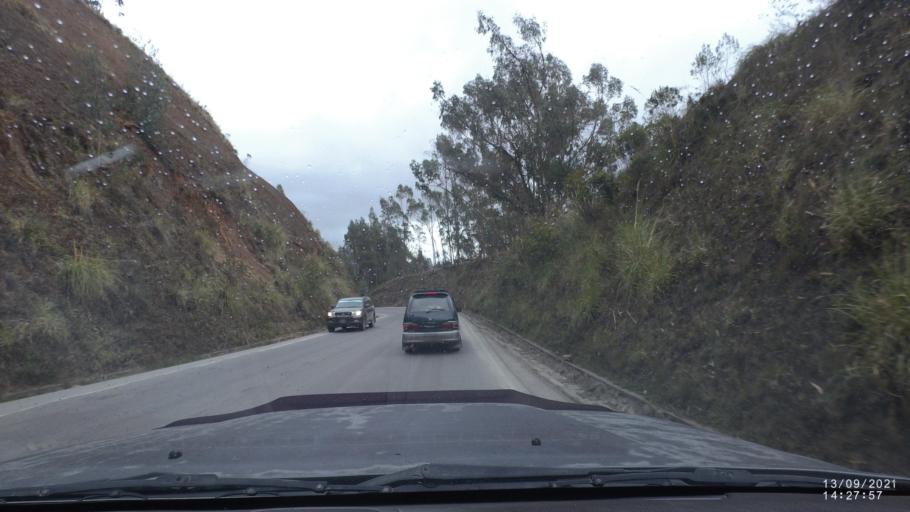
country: BO
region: Cochabamba
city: Colomi
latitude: -17.3167
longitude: -65.8621
